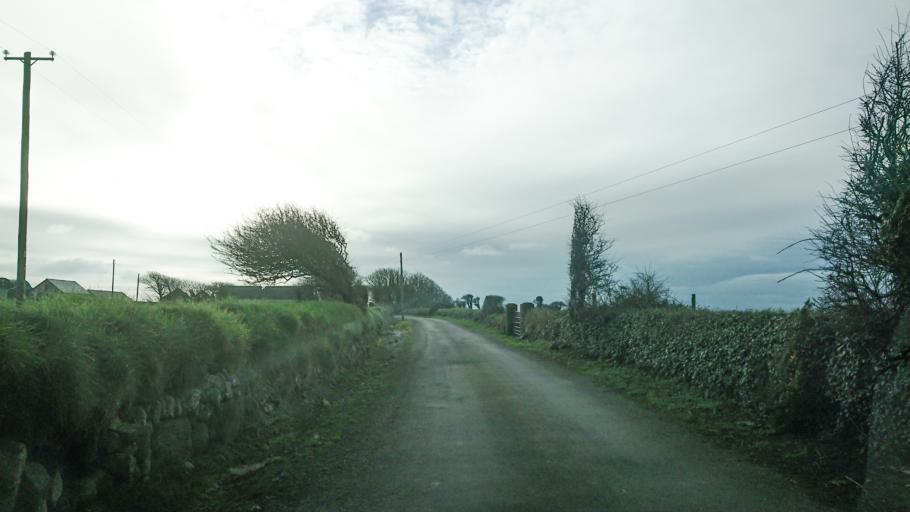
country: IE
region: Munster
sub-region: Waterford
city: Tra Mhor
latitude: 52.1411
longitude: -7.1948
